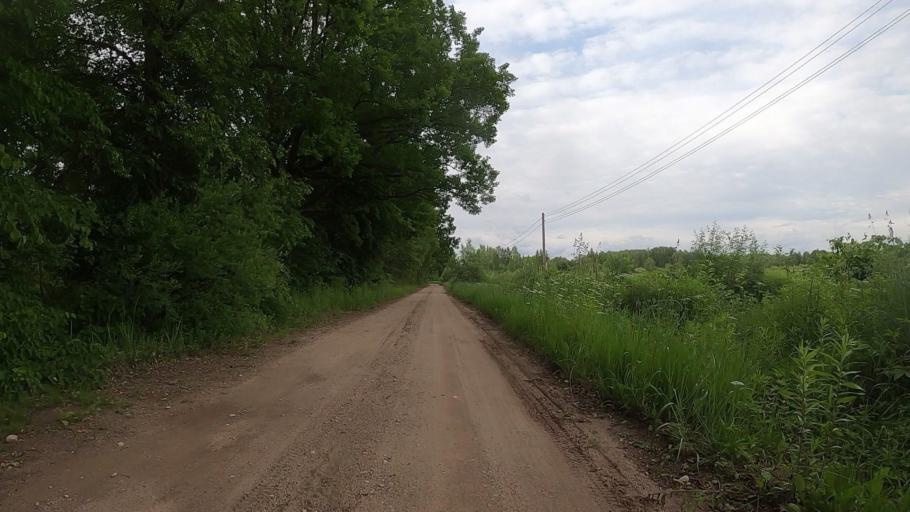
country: LV
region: Ozolnieku
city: Ozolnieki
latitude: 56.7199
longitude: 23.7894
